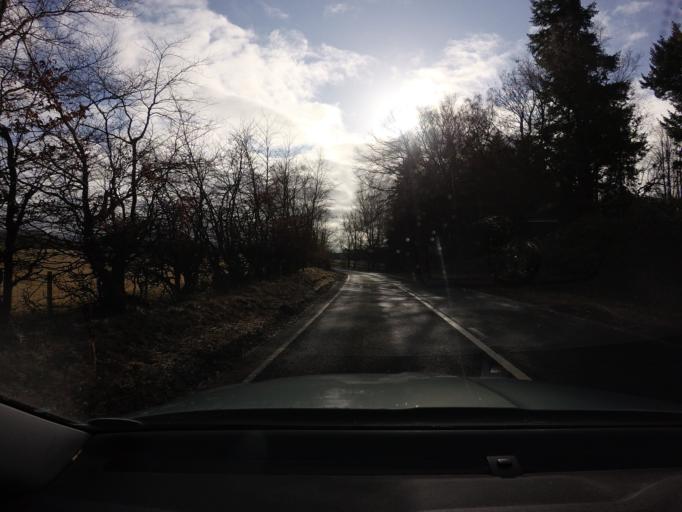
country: GB
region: Scotland
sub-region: South Lanarkshire
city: Forth
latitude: 55.7031
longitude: -3.7172
